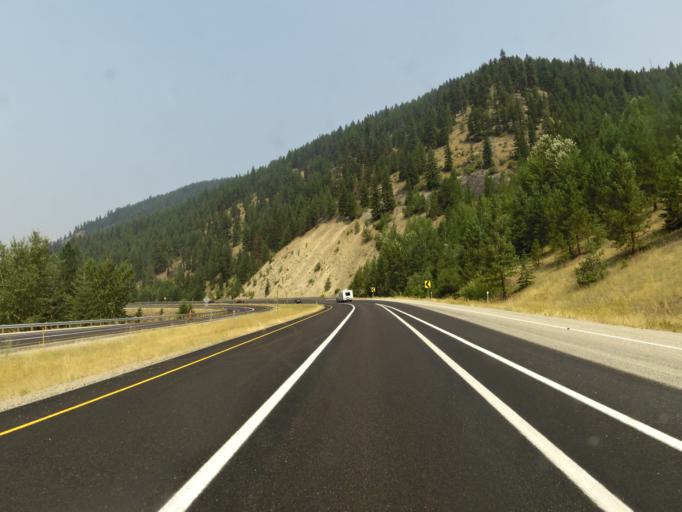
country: US
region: Montana
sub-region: Sanders County
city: Thompson Falls
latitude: 47.3250
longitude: -115.2496
